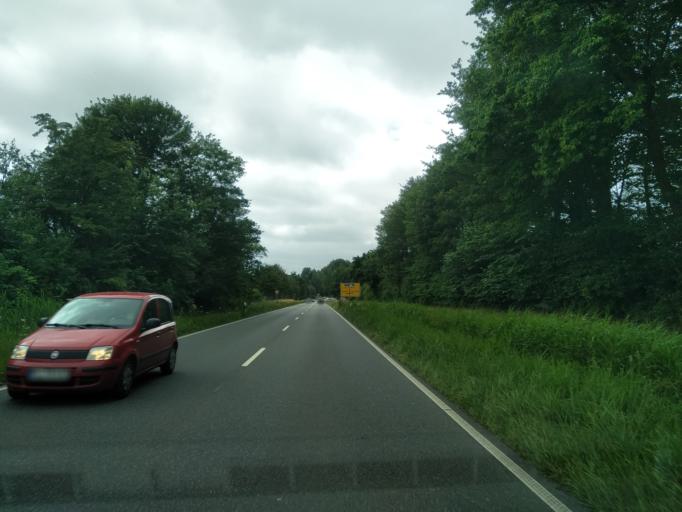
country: DE
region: Schleswig-Holstein
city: Munkbrarup
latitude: 54.8030
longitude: 9.5414
